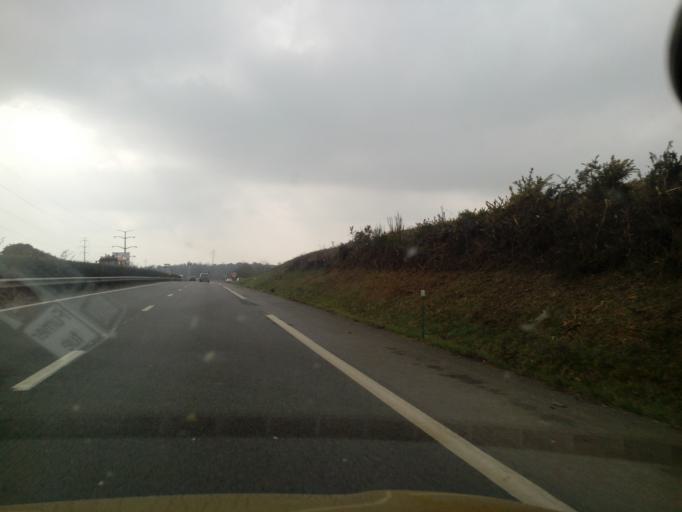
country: FR
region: Brittany
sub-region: Departement du Morbihan
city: Saint-Nolff
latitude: 47.6949
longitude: -2.6334
